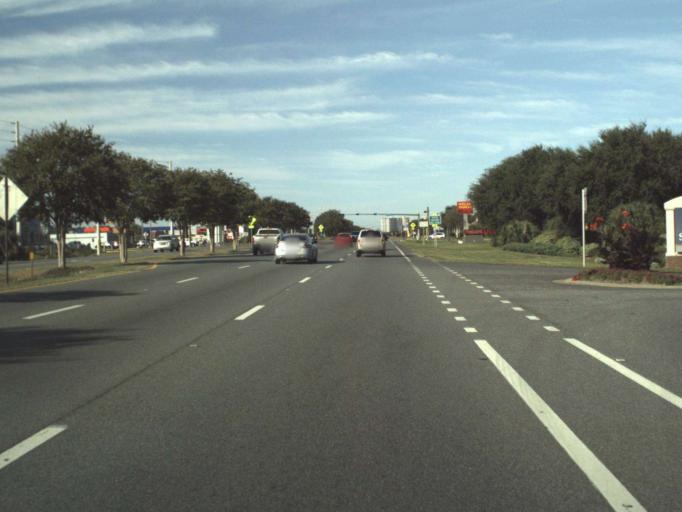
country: US
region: Florida
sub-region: Okaloosa County
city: Destin
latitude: 30.3887
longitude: -86.4283
